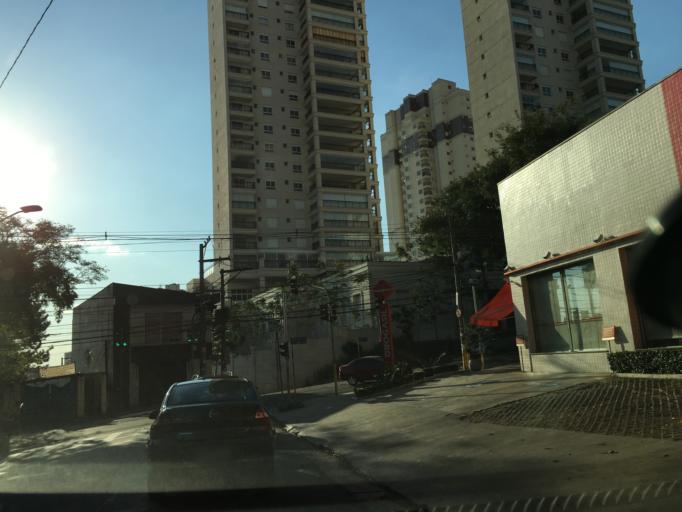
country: BR
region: Sao Paulo
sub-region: Sao Paulo
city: Sao Paulo
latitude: -23.4964
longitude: -46.6366
